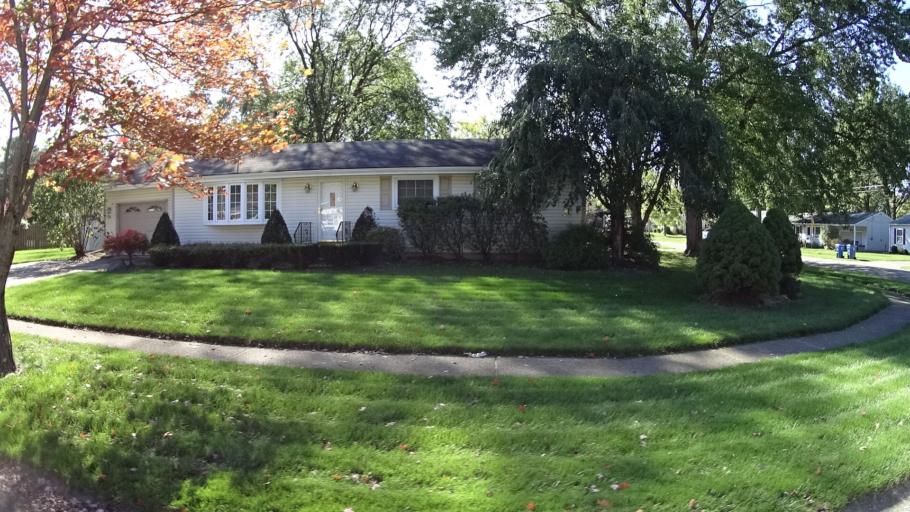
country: US
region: Ohio
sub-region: Lorain County
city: Lorain
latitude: 41.4166
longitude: -82.1733
